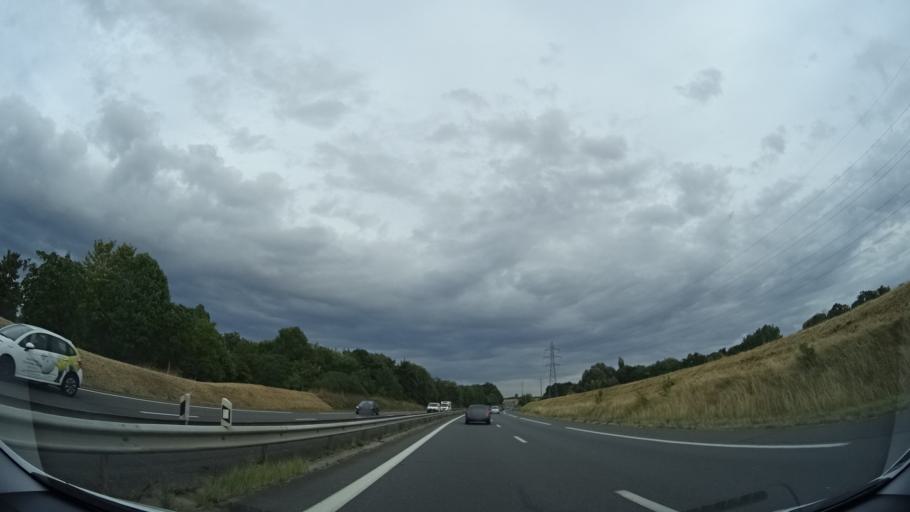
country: FR
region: Centre
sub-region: Departement du Loiret
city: Boigny-sur-Bionne
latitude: 47.9196
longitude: 2.0025
